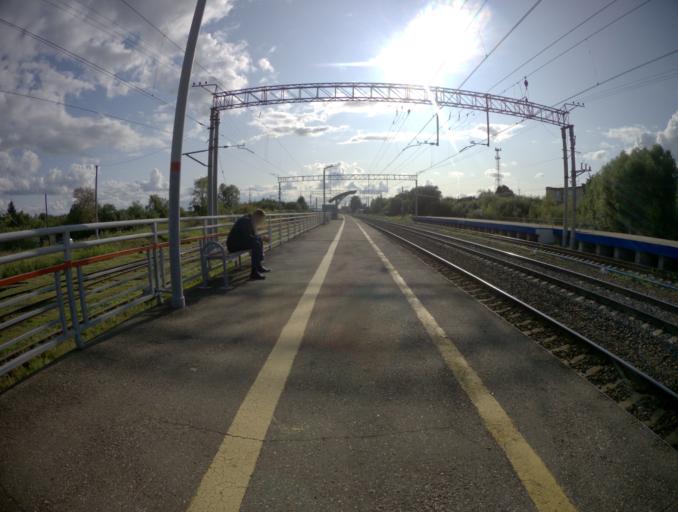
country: RU
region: Vladimir
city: Lakinsk
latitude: 56.0196
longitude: 39.9808
